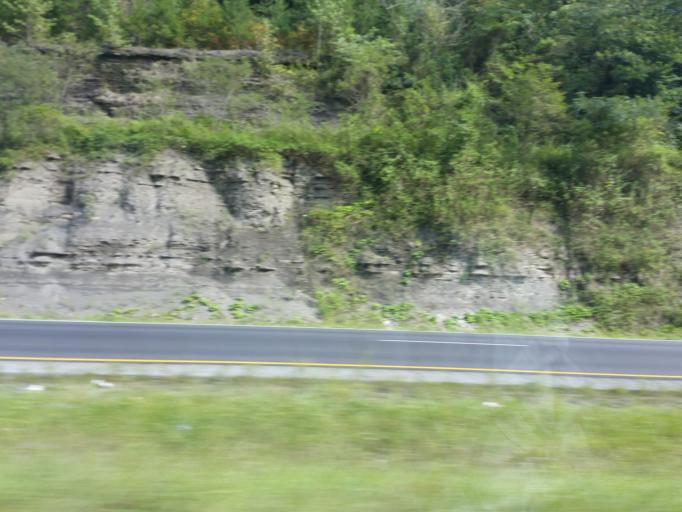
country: US
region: Kentucky
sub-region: Bell County
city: Pineville
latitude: 36.7159
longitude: -83.6903
